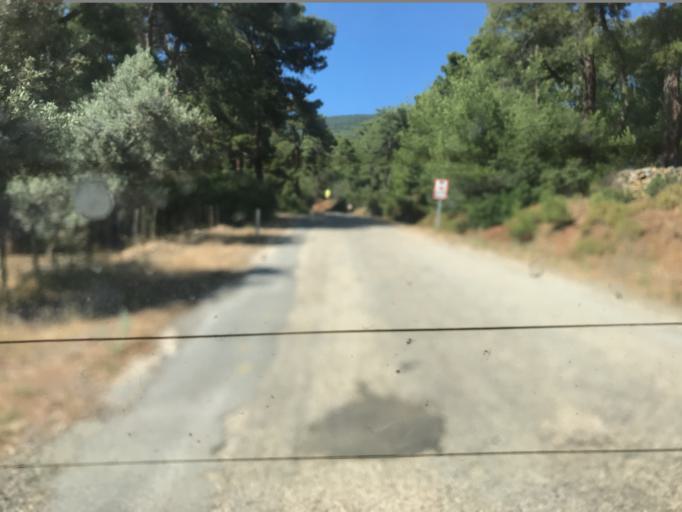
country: TR
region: Mugla
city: Kiulukioi
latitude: 37.3654
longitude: 27.4969
